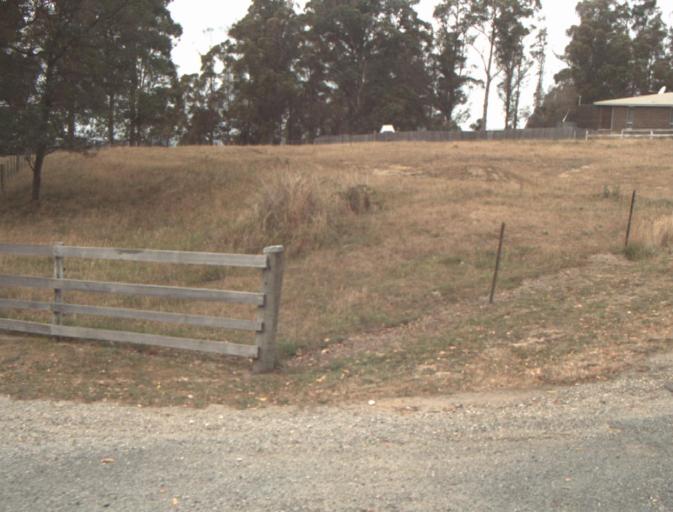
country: AU
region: Tasmania
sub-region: Launceston
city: Mayfield
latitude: -41.2010
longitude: 147.2178
